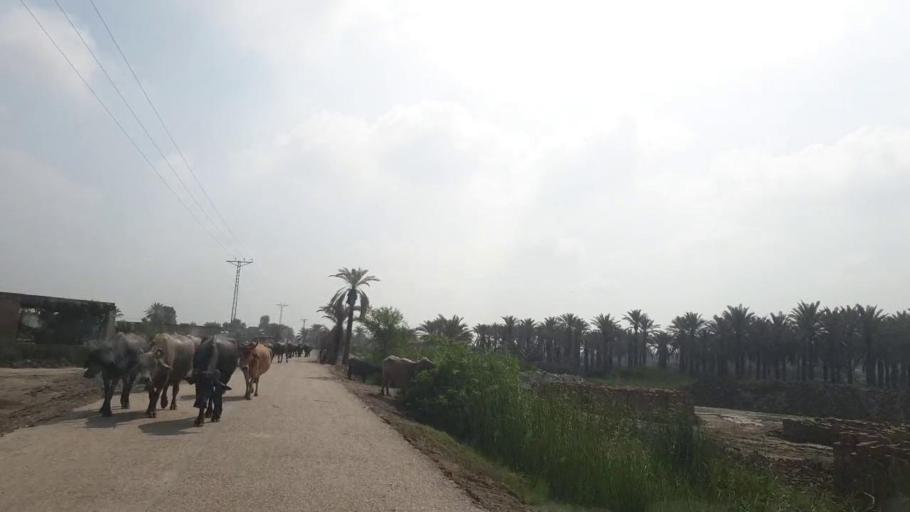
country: PK
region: Sindh
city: Khairpur
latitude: 27.5734
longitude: 68.7657
